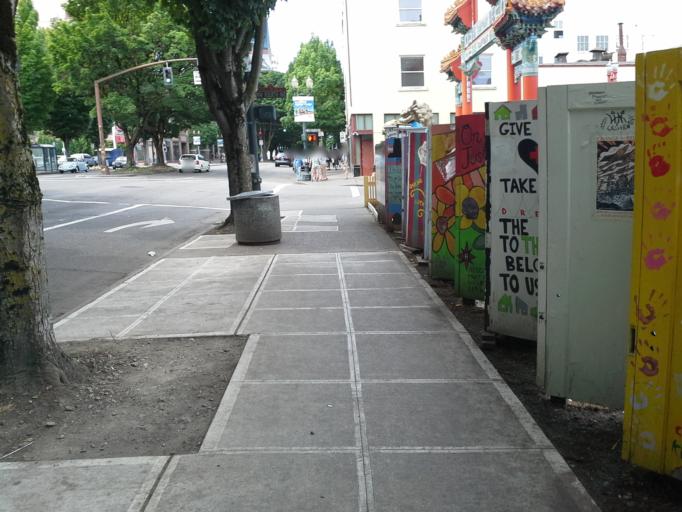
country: US
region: Oregon
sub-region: Multnomah County
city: Portland
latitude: 45.5233
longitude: -122.6739
